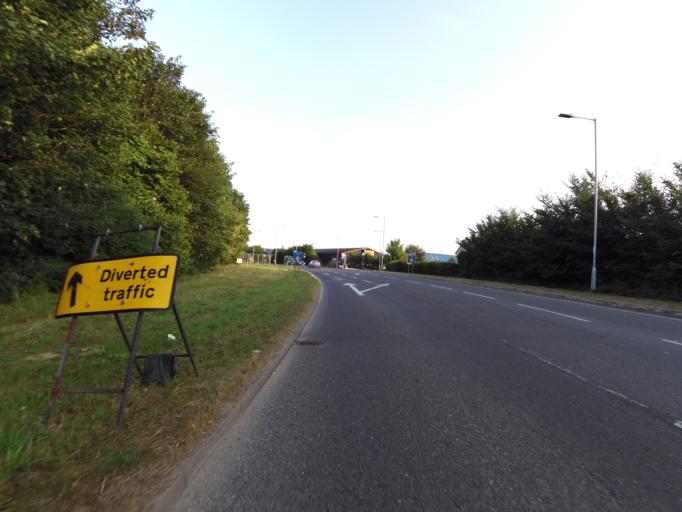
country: GB
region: England
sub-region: Suffolk
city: Needham Market
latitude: 52.1461
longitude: 1.0635
